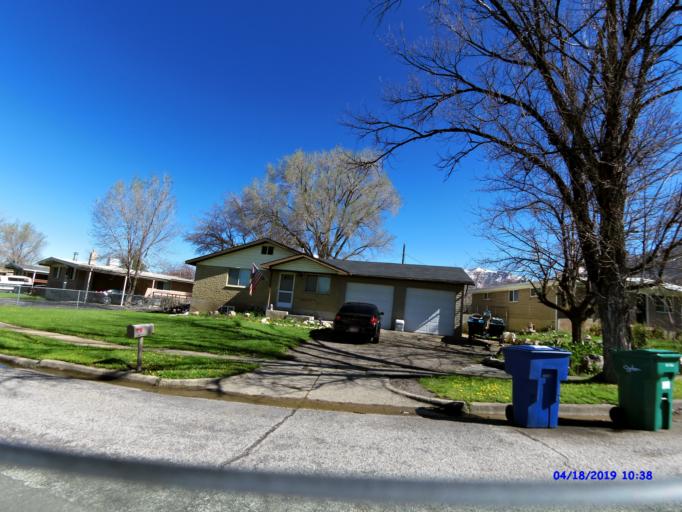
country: US
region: Utah
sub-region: Weber County
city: Harrisville
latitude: 41.2713
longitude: -111.9614
